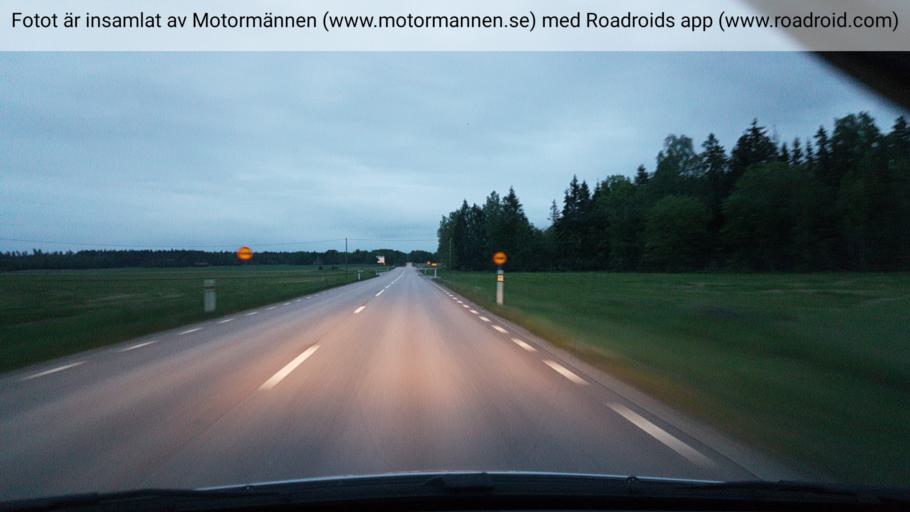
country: SE
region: Vaestmanland
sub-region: Sala Kommun
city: Sala
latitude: 59.8249
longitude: 16.7408
